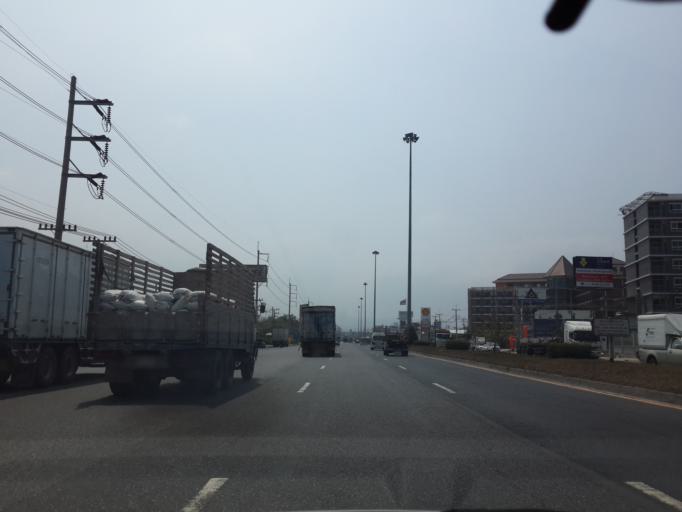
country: TH
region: Chon Buri
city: Chon Buri
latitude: 13.4163
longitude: 100.9984
